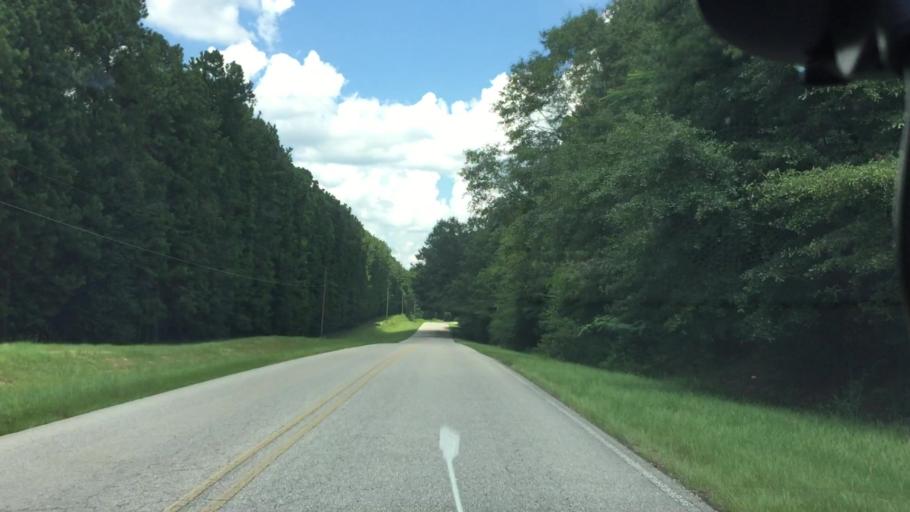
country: US
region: Alabama
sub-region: Pike County
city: Troy
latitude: 31.7646
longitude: -85.9824
